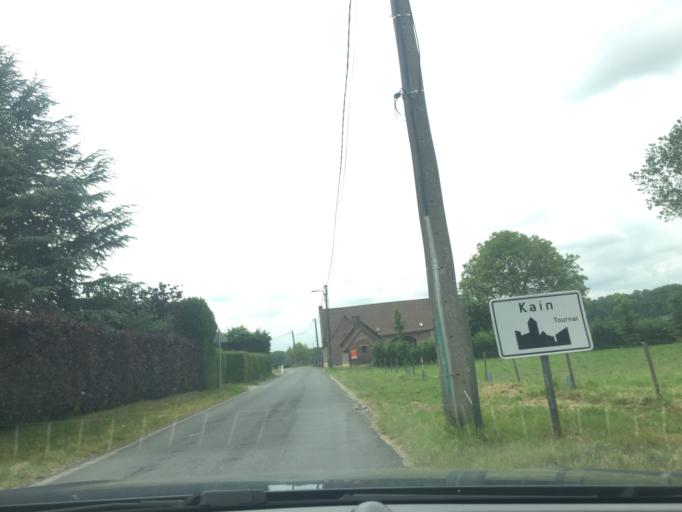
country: BE
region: Wallonia
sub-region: Province du Hainaut
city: Pecq
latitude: 50.6454
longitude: 3.3562
